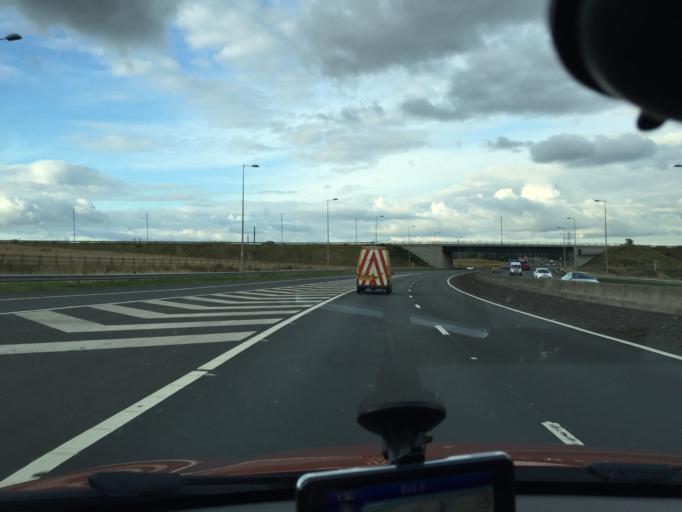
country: GB
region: Scotland
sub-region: North Lanarkshire
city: Glenboig
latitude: 55.9181
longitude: -4.0642
